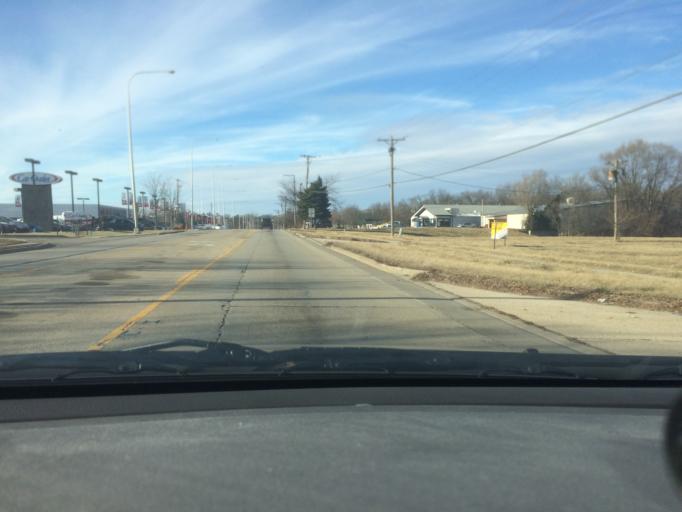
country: US
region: Illinois
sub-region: Kane County
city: Elgin
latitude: 42.0335
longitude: -88.2532
